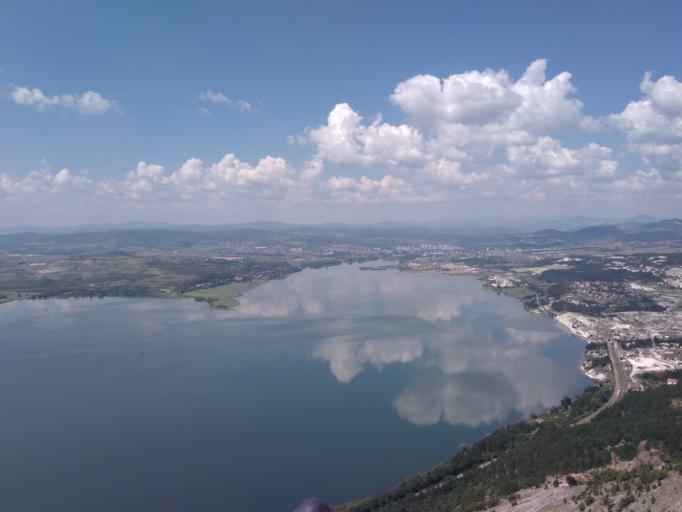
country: BG
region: Kurdzhali
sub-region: Obshtina Kurdzhali
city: Kurdzhali
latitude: 41.6232
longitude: 25.4576
